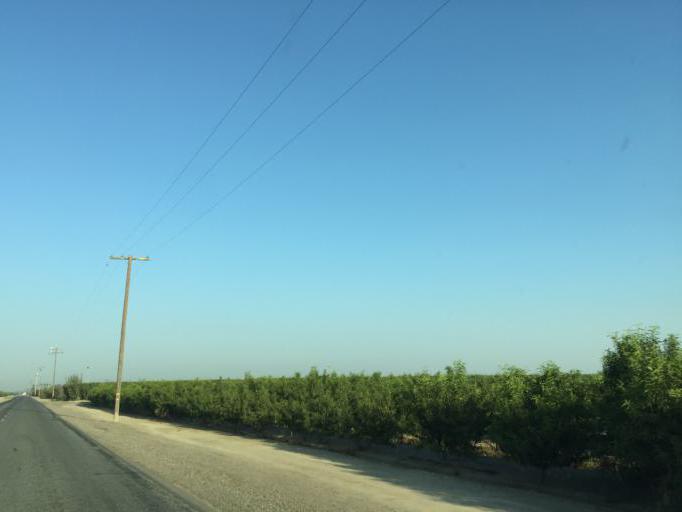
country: US
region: California
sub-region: Tulare County
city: London
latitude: 36.4589
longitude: -119.4463
